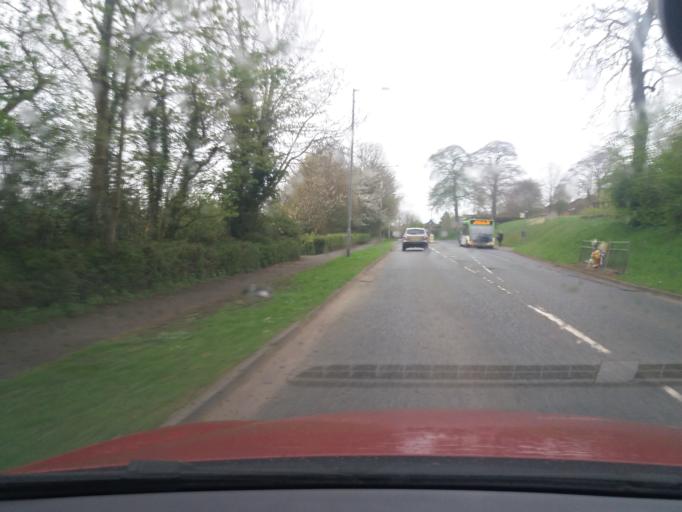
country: GB
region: England
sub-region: Lancashire
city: Clayton-le-Woods
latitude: 53.7000
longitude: -2.6343
